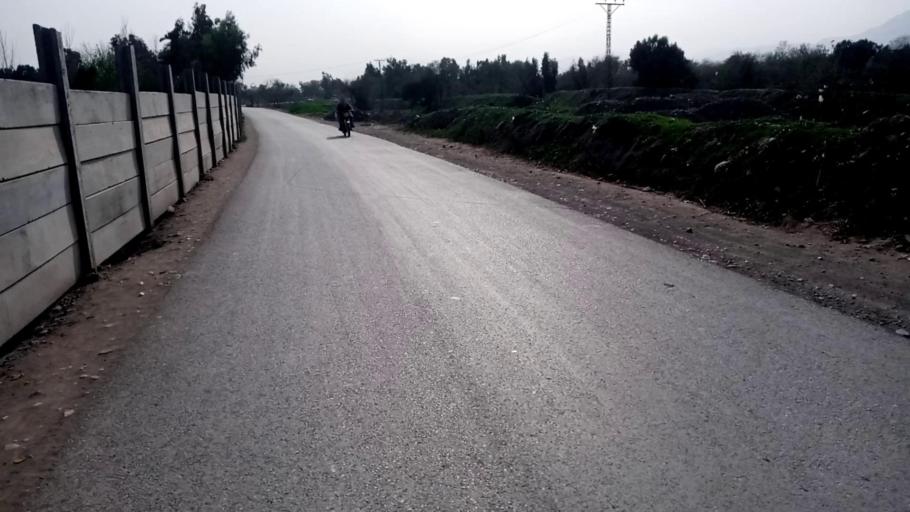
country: PK
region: Khyber Pakhtunkhwa
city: Peshawar
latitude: 34.0242
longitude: 71.4493
